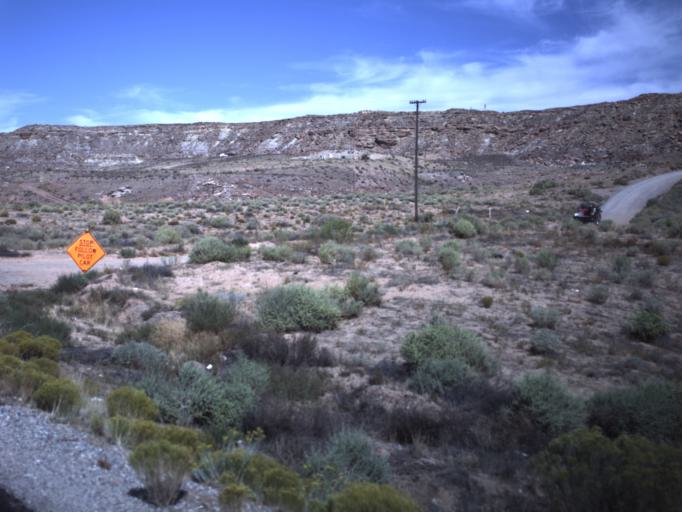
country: US
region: Utah
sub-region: San Juan County
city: Blanding
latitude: 37.2315
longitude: -109.2167
